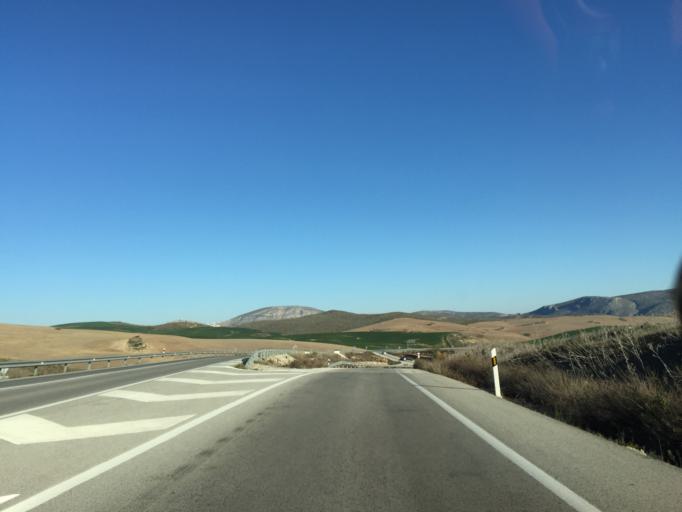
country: ES
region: Andalusia
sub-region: Provincia de Malaga
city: Ardales
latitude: 36.9376
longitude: -4.8647
